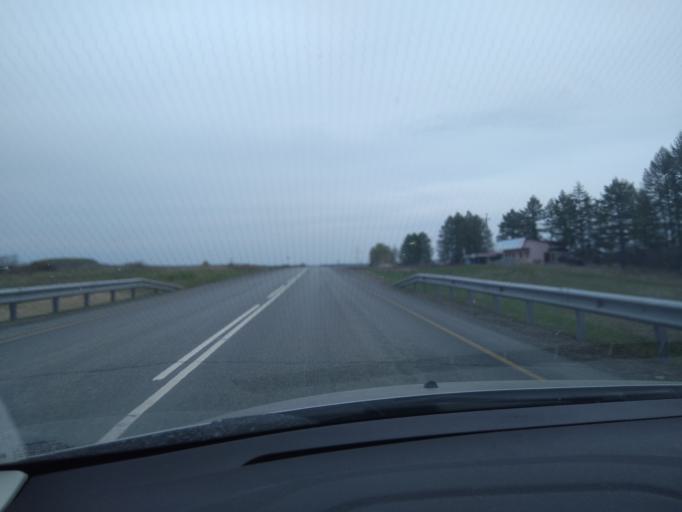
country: RU
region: Sverdlovsk
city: Talitsa
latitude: 57.0716
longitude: 63.5921
